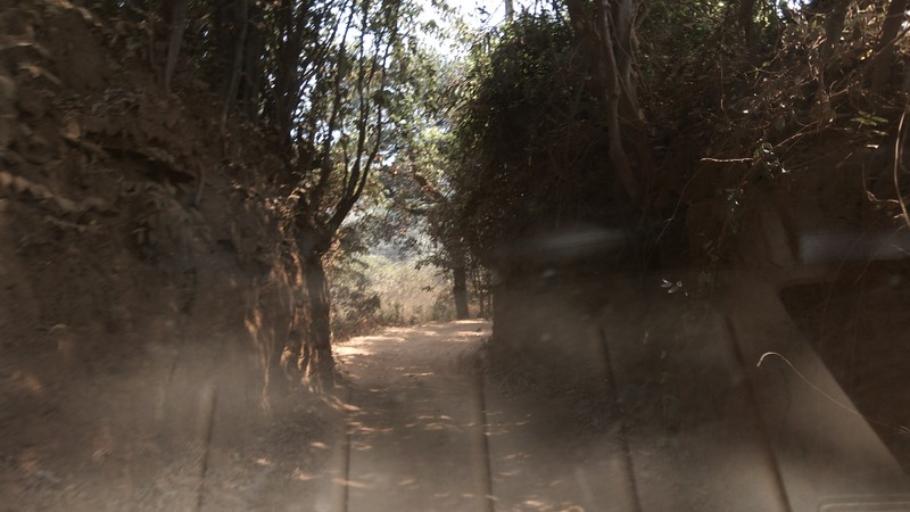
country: IN
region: Goa
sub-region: South Goa
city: Sanguem
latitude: 15.3117
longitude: 74.2982
